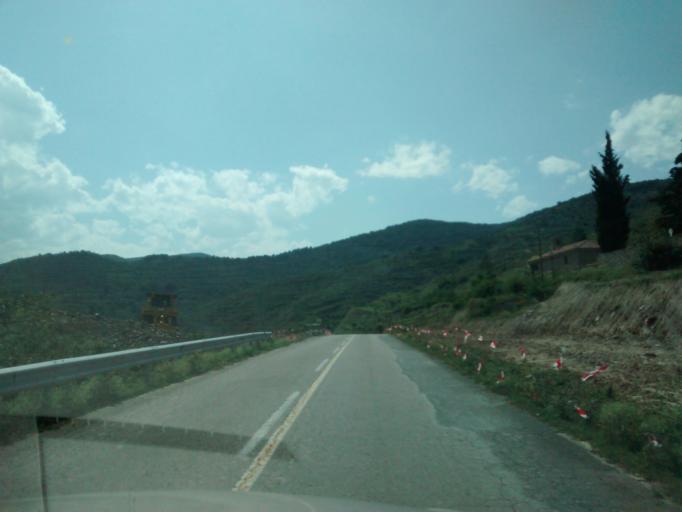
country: ES
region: La Rioja
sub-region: Provincia de La Rioja
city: Terroba
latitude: 42.2571
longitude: -2.4465
